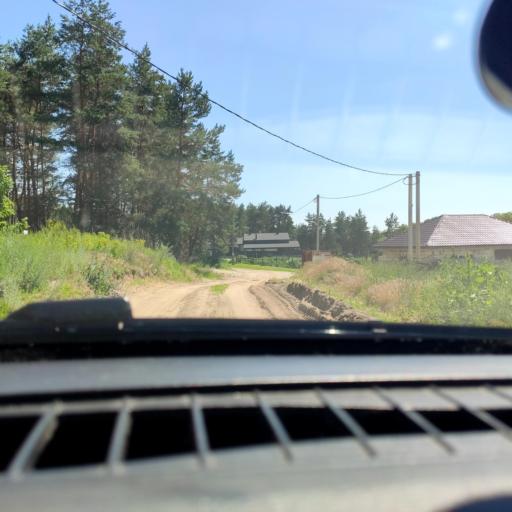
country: RU
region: Voronezj
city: Podgornoye
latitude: 51.7974
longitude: 39.1359
